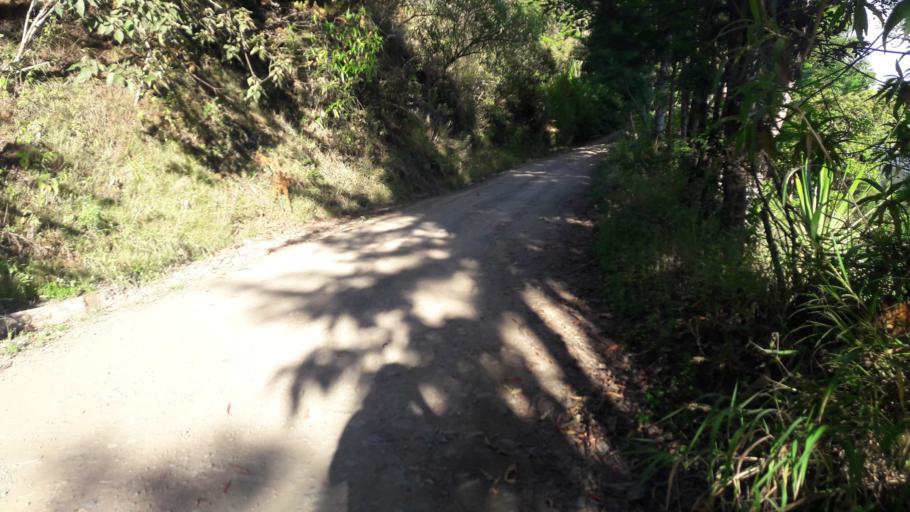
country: CO
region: Cundinamarca
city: Tenza
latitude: 5.0910
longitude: -73.4248
